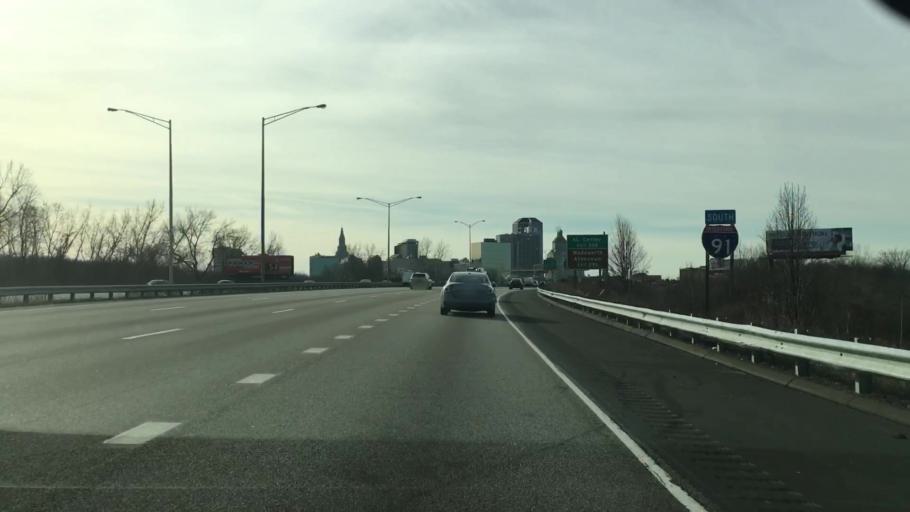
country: US
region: Connecticut
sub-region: Hartford County
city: Hartford
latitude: 41.7807
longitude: -72.6606
